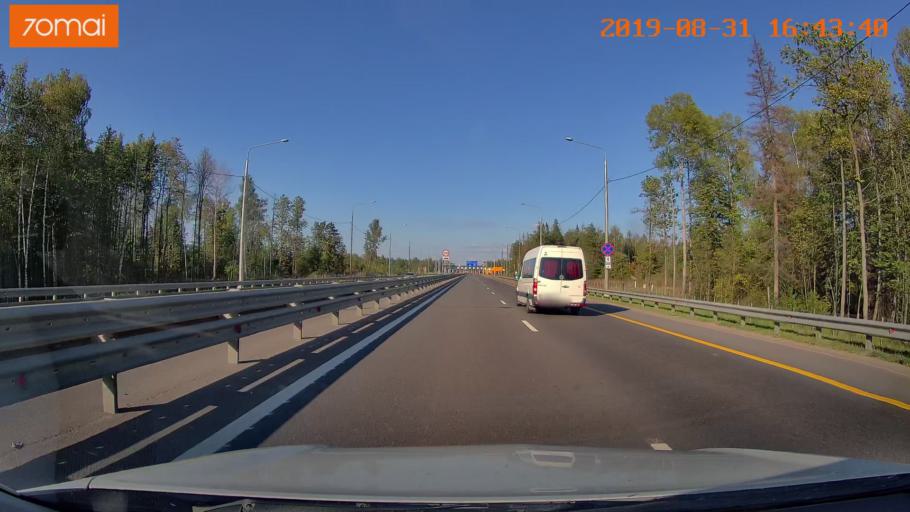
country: RU
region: Kaluga
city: Mstikhino
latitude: 54.6127
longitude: 36.1087
